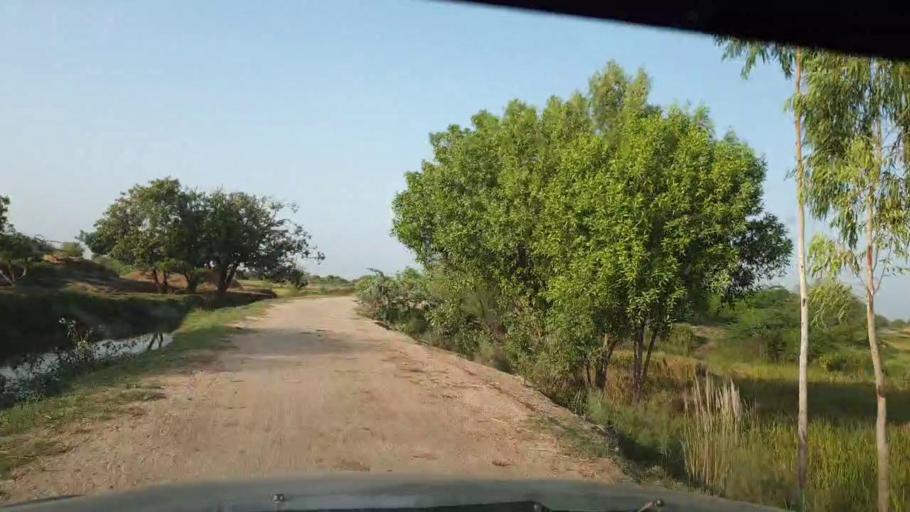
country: PK
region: Sindh
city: Rajo Khanani
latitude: 25.0267
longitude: 68.7715
